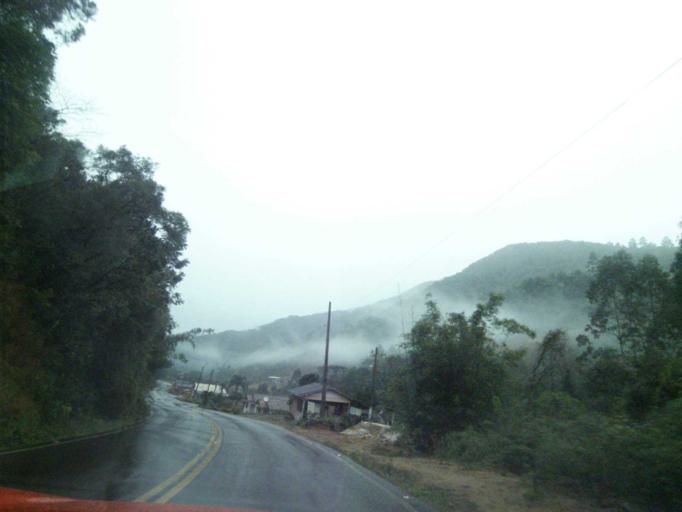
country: BR
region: Santa Catarina
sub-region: Anitapolis
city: Anitapolis
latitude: -27.8299
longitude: -49.0510
